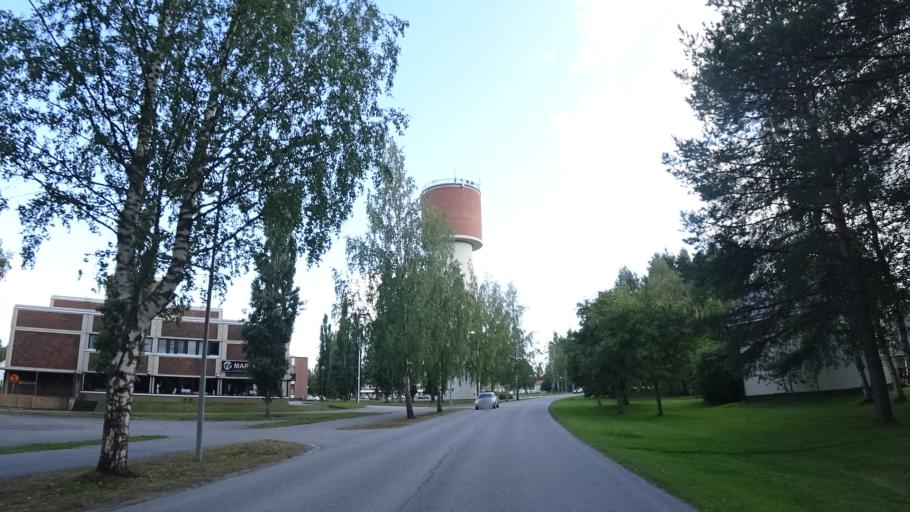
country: FI
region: North Karelia
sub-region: Pielisen Karjala
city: Lieksa
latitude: 63.3227
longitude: 30.0227
